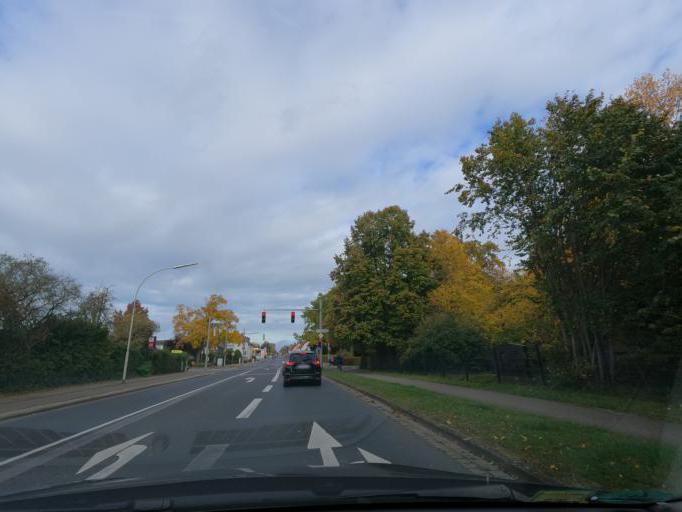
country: DE
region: Lower Saxony
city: Leiferde
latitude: 52.2189
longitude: 10.5020
